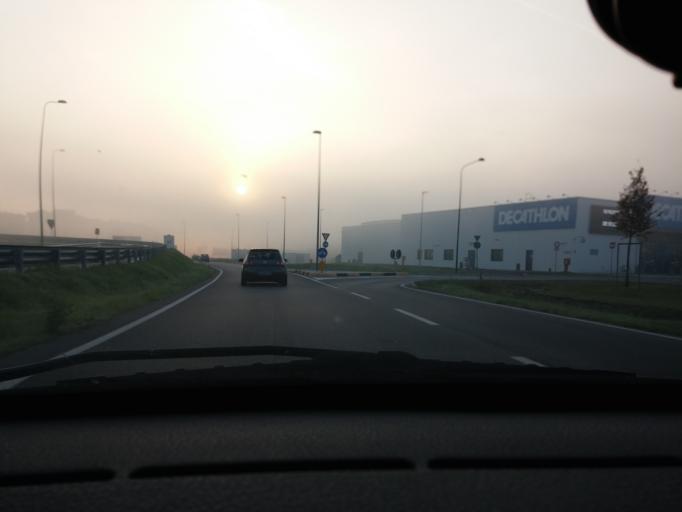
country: IT
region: Emilia-Romagna
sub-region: Provincia di Ferrara
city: Ferrara
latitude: 44.8231
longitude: 11.5900
